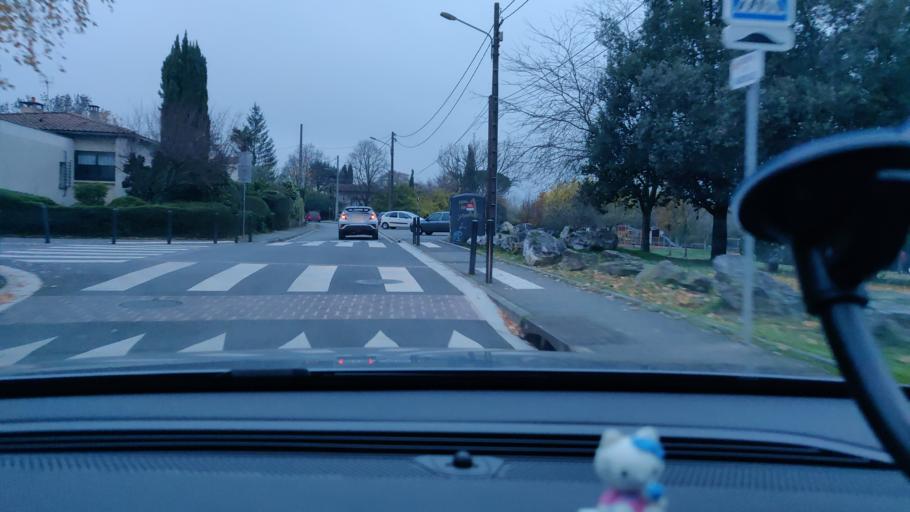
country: FR
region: Midi-Pyrenees
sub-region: Departement de la Haute-Garonne
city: Ramonville-Saint-Agne
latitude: 43.5500
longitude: 1.4549
